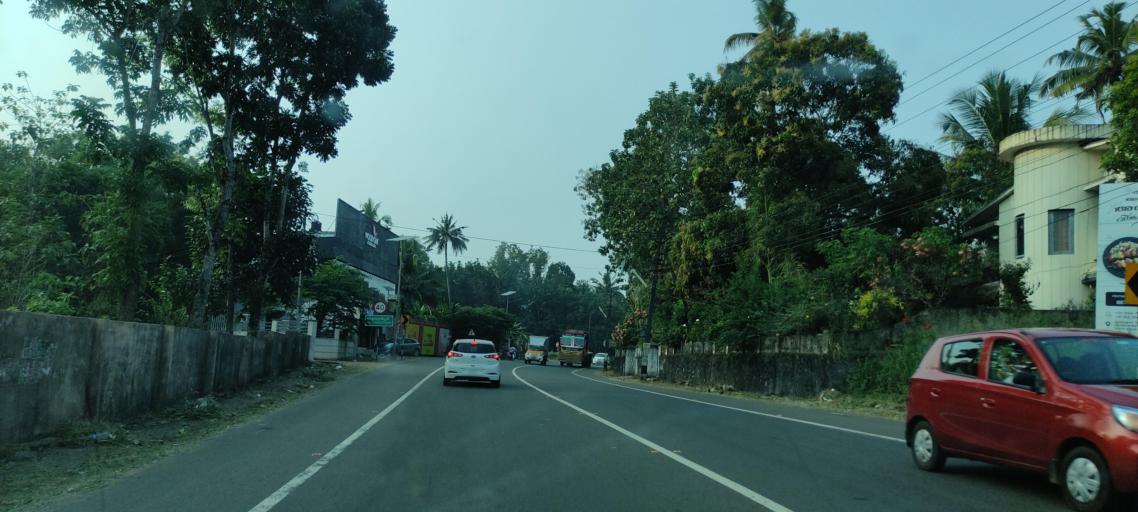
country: IN
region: Kerala
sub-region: Pattanamtitta
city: Adur
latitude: 9.1417
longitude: 76.7341
